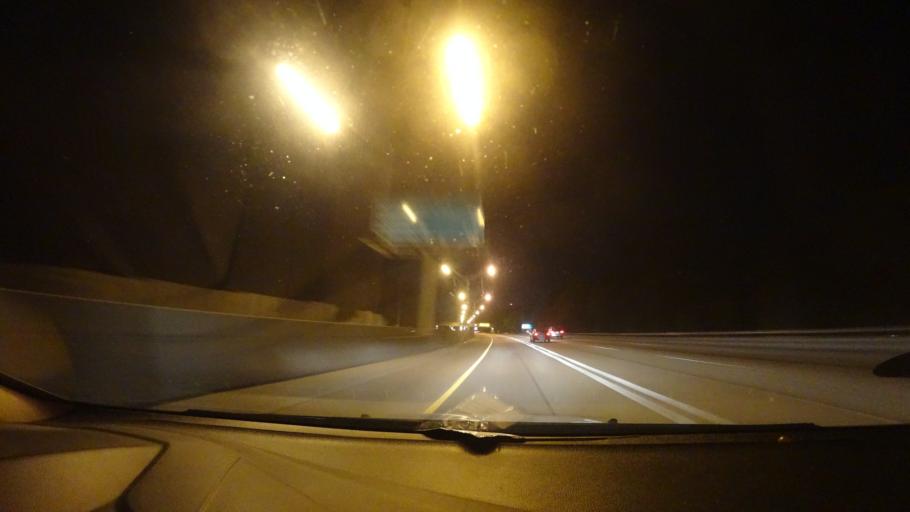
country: US
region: Georgia
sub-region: DeKalb County
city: Panthersville
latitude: 33.7122
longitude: -84.2895
